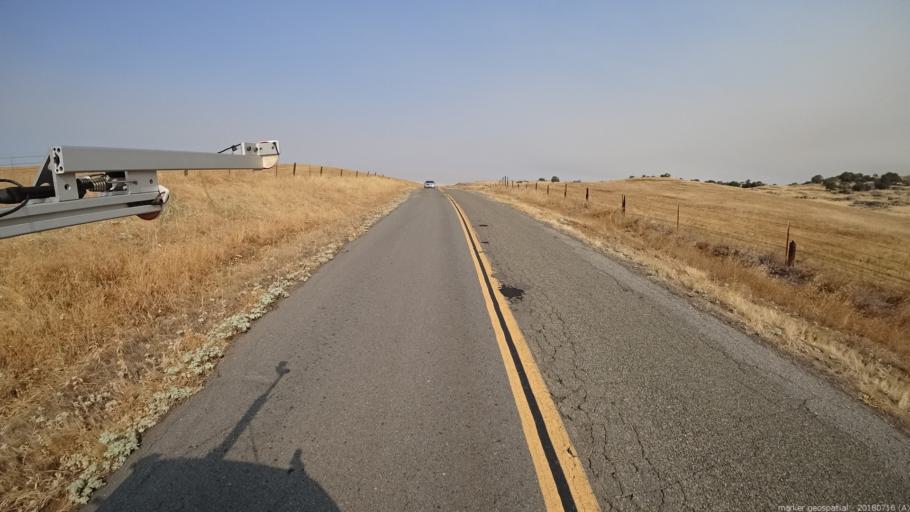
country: US
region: California
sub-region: Madera County
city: Bonadelle Ranchos-Madera Ranchos
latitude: 37.1204
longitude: -119.9375
